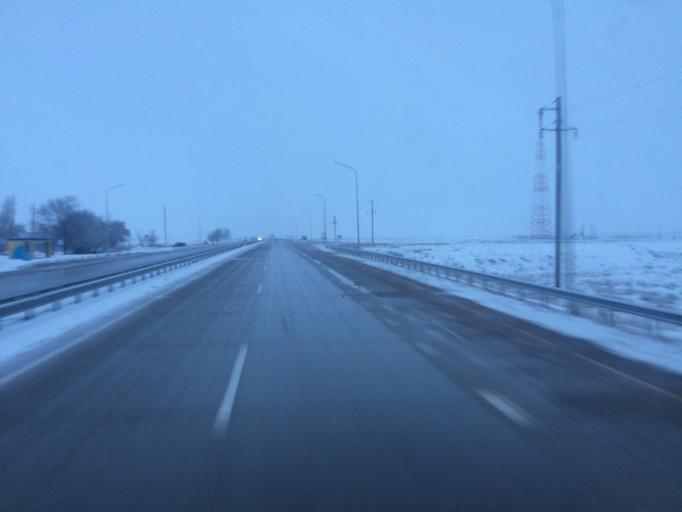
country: KZ
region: Zhambyl
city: Kulan
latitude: 42.9717
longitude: 72.4131
